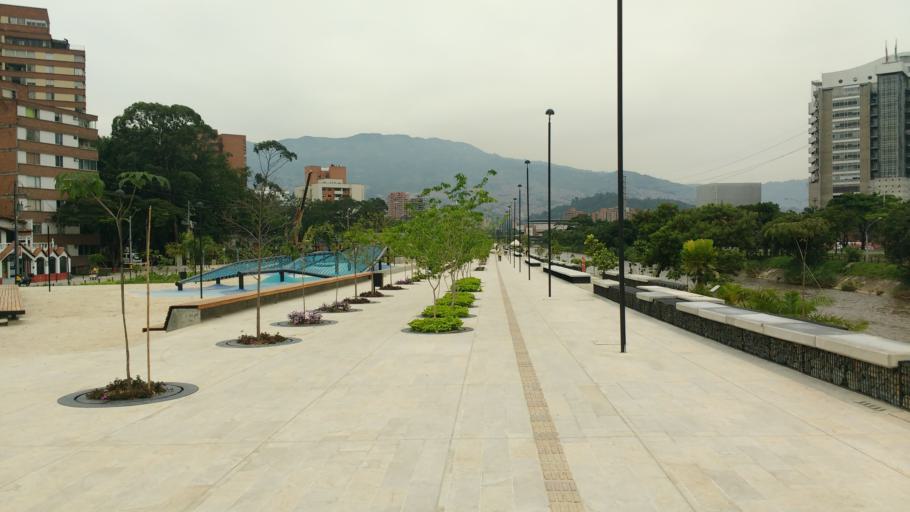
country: CO
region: Antioquia
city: Medellin
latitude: 6.2417
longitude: -75.5785
